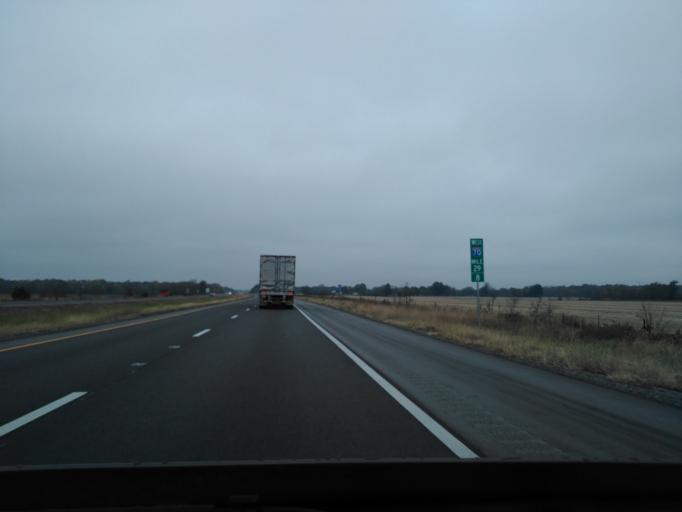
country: US
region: Illinois
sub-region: Madison County
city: Highland
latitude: 38.7866
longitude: -89.6387
